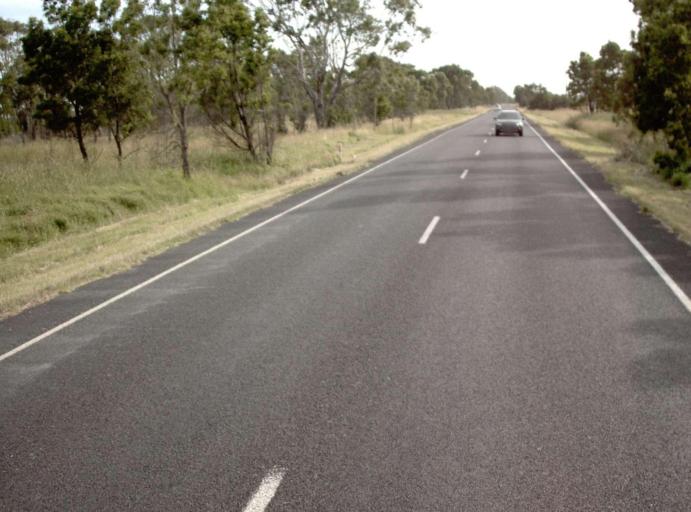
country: AU
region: Victoria
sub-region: Latrobe
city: Traralgon
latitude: -38.0871
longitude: 146.6037
